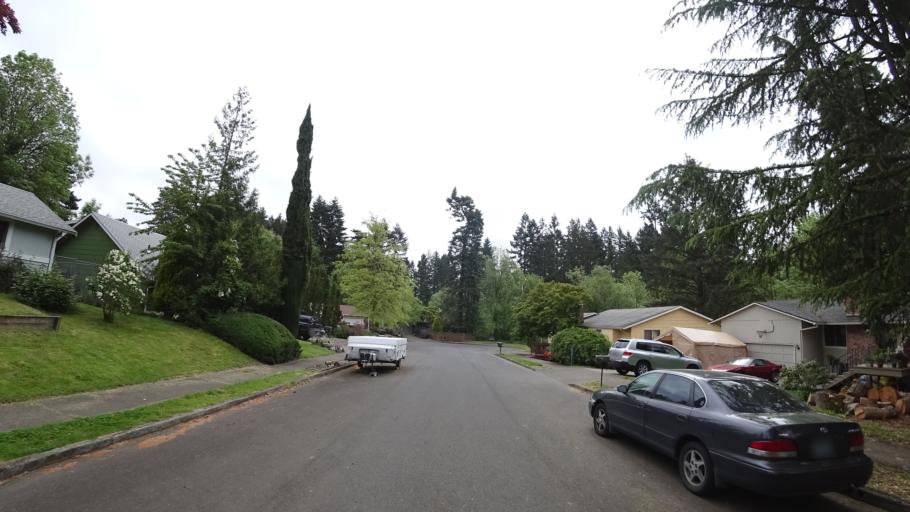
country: US
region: Oregon
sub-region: Washington County
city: Aloha
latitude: 45.5194
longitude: -122.8639
